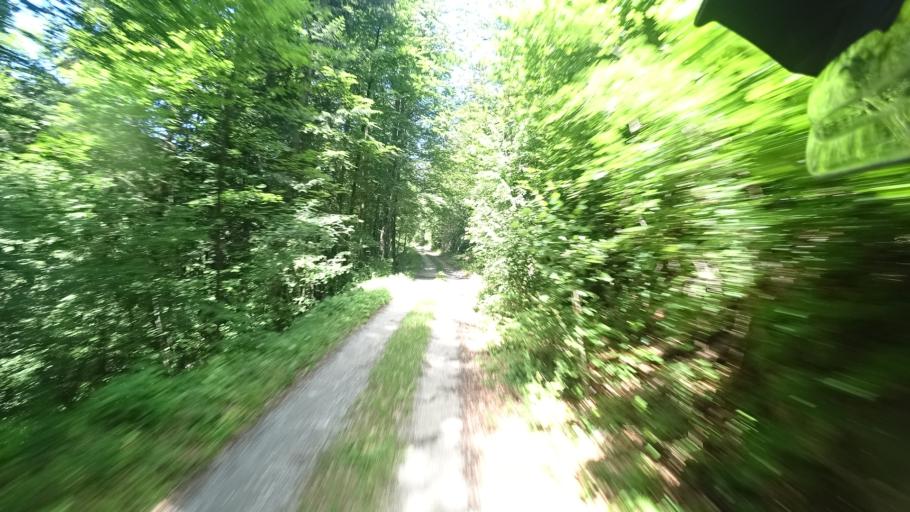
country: SI
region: Osilnica
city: Osilnica
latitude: 45.4732
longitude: 14.7240
